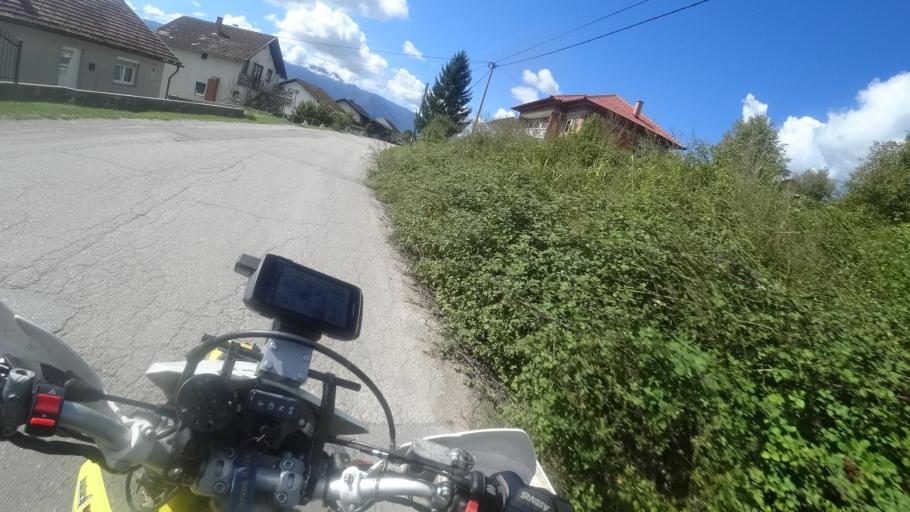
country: BA
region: Federation of Bosnia and Herzegovina
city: Bihac
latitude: 44.8125
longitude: 15.9047
